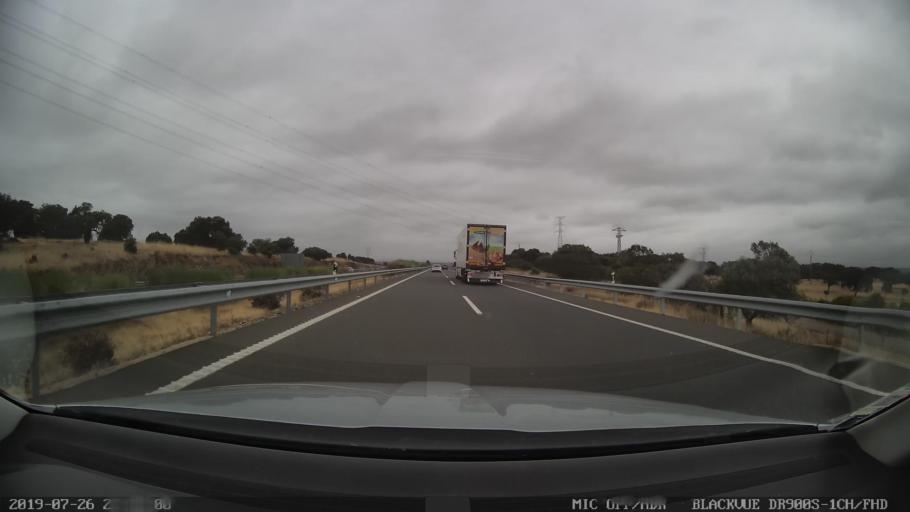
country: ES
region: Extremadura
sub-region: Provincia de Caceres
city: Jaraicejo
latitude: 39.5793
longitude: -5.8345
